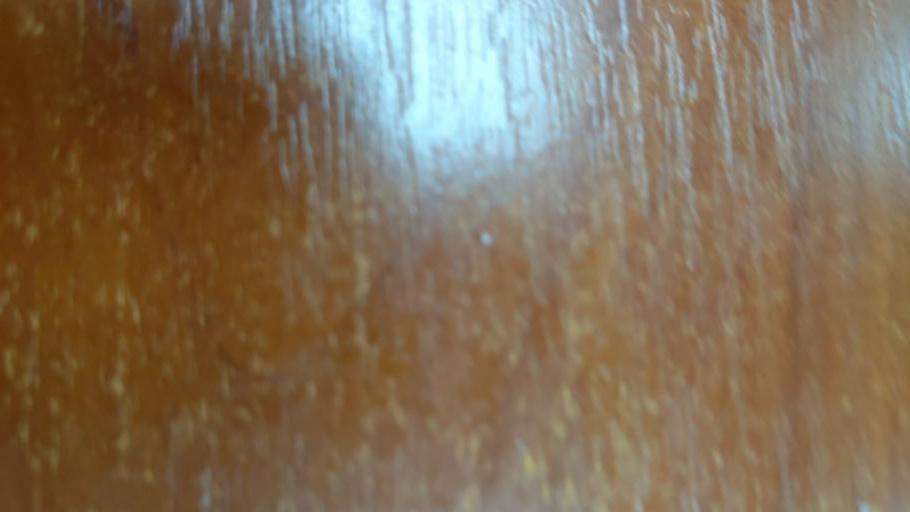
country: RU
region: Moskovskaya
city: Aprelevka
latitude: 55.5417
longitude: 37.0931
